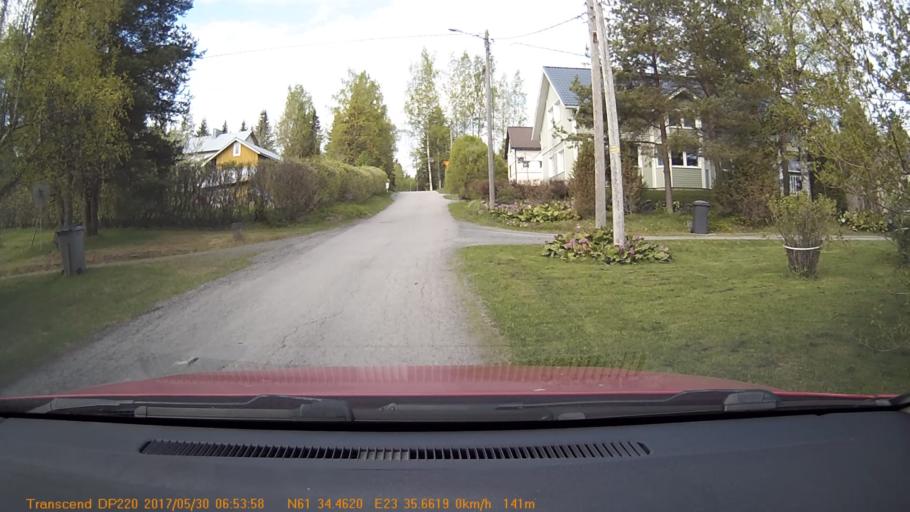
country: FI
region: Pirkanmaa
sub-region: Tampere
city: Yloejaervi
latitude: 61.5744
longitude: 23.5944
